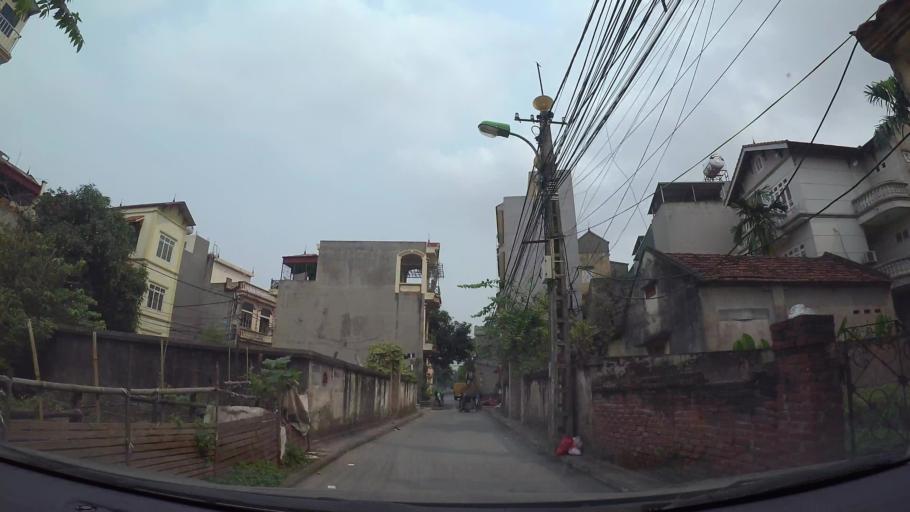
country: VN
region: Ha Noi
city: Trau Quy
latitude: 21.0591
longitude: 105.8997
